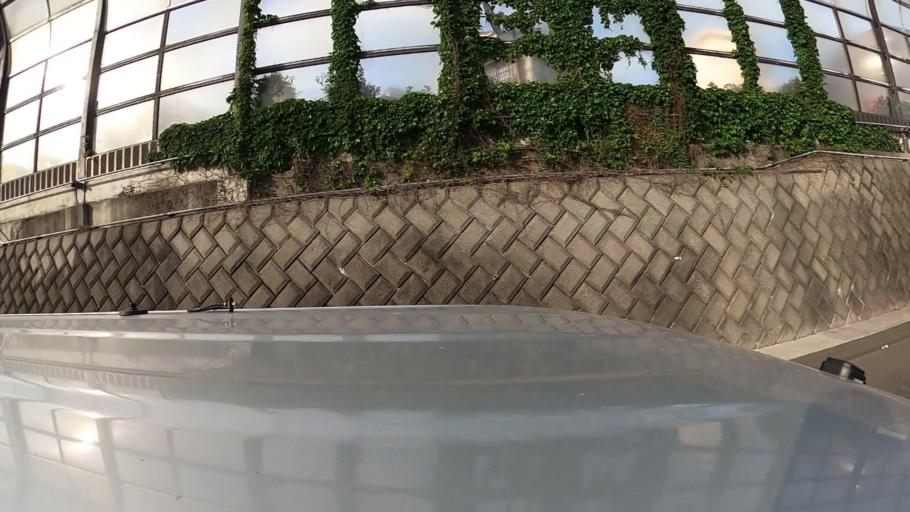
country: JP
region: Saitama
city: Asaka
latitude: 35.7674
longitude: 139.5739
